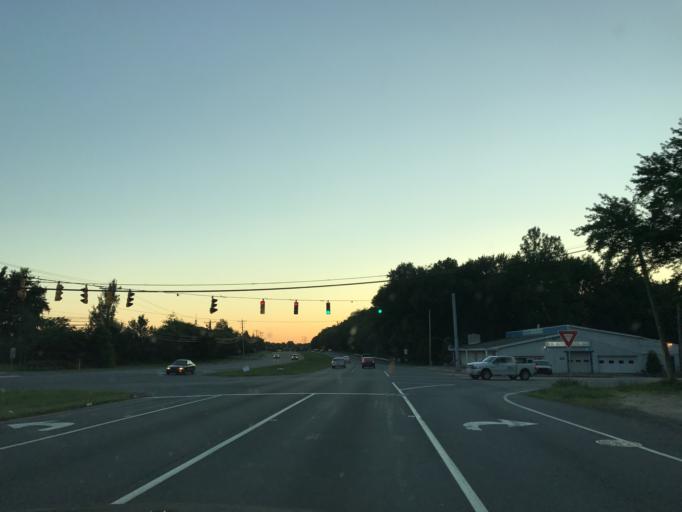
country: US
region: Delaware
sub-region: New Castle County
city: Glasgow
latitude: 39.6049
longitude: -75.7685
